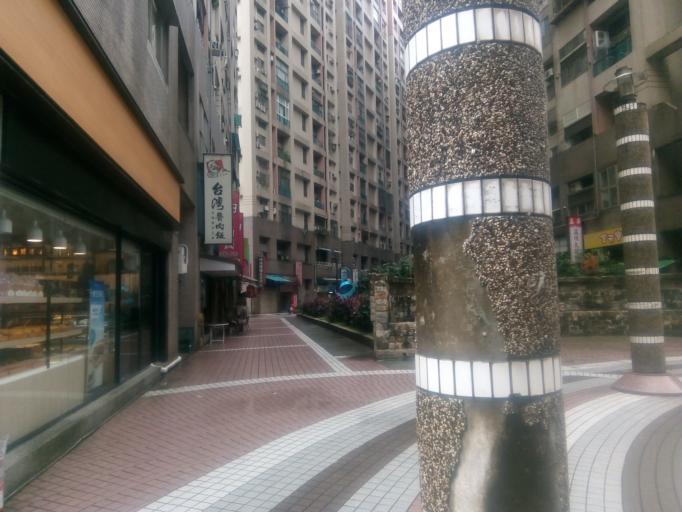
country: TW
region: Taiwan
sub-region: Keelung
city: Keelung
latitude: 25.0733
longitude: 121.6622
